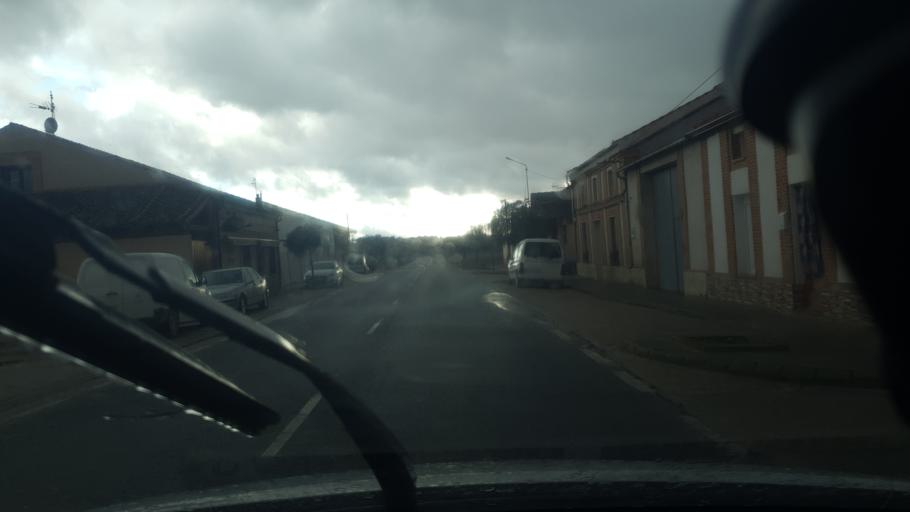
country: ES
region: Castille and Leon
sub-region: Provincia de Segovia
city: Samboal
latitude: 41.2984
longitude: -4.4080
